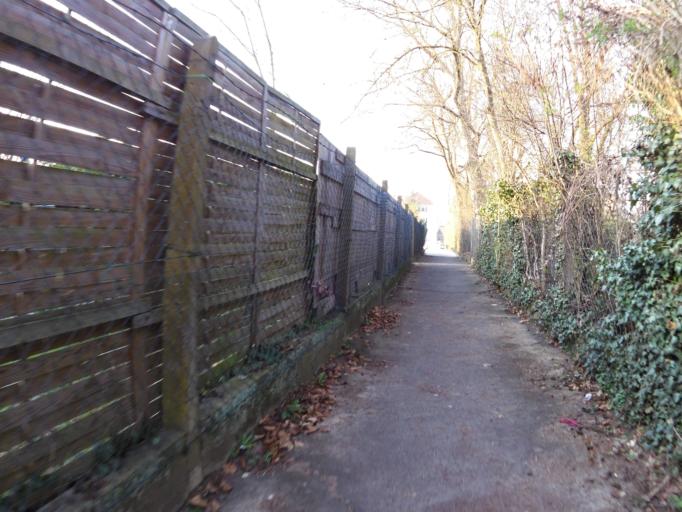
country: DE
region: Bavaria
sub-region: Regierungsbezirk Unterfranken
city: Kitzingen
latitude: 49.7309
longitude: 10.1568
